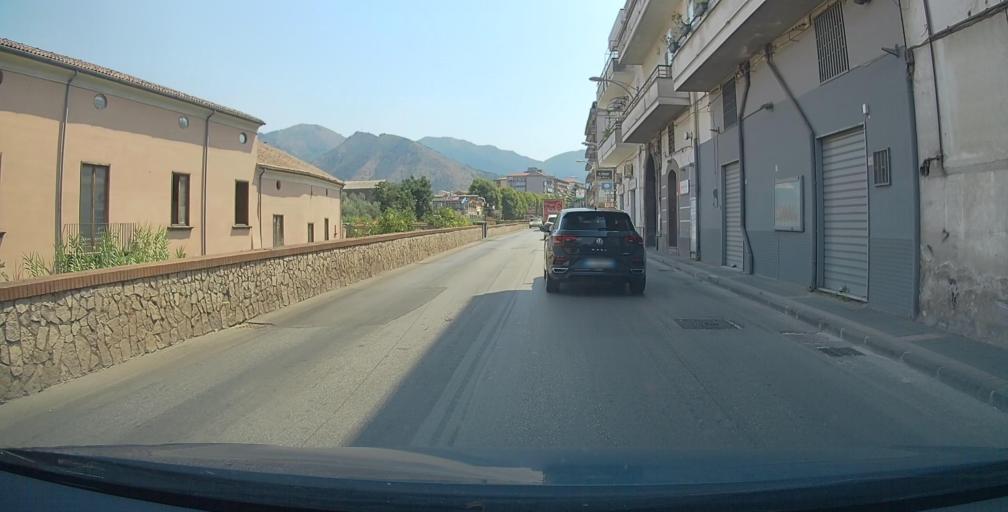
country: IT
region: Campania
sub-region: Provincia di Salerno
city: Nocera Superiore
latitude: 40.7403
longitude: 14.6660
